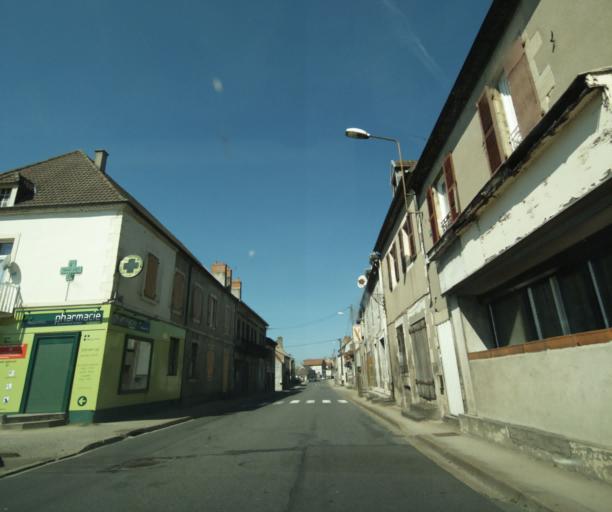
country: FR
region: Auvergne
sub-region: Departement de l'Allier
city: Trevol
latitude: 46.6590
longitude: 3.2495
